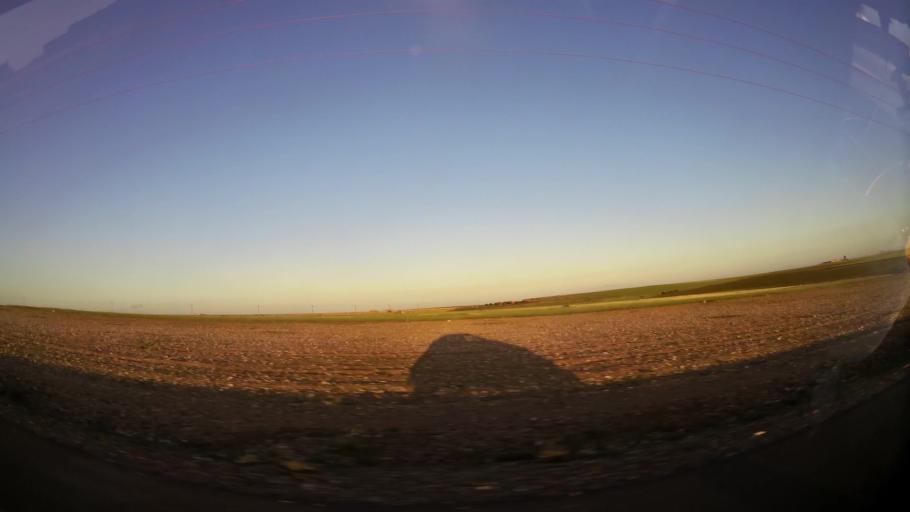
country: MA
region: Marrakech-Tensift-Al Haouz
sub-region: Kelaa-Des-Sraghna
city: Sidi Abdallah
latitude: 32.2364
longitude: -7.9285
